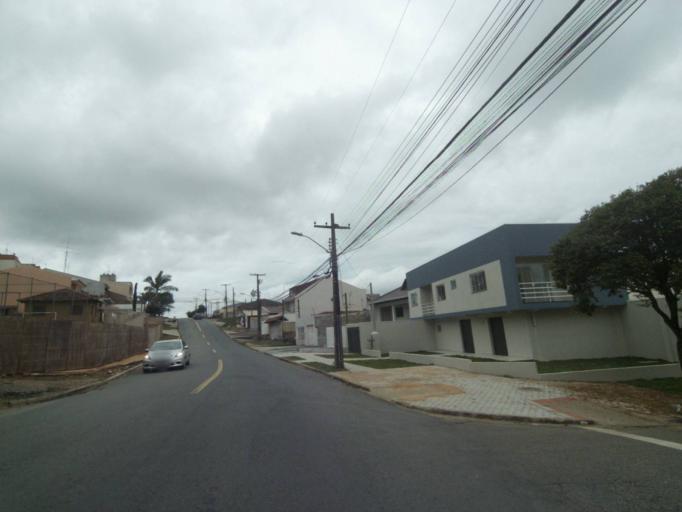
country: BR
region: Parana
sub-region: Curitiba
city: Curitiba
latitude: -25.4583
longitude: -49.3216
